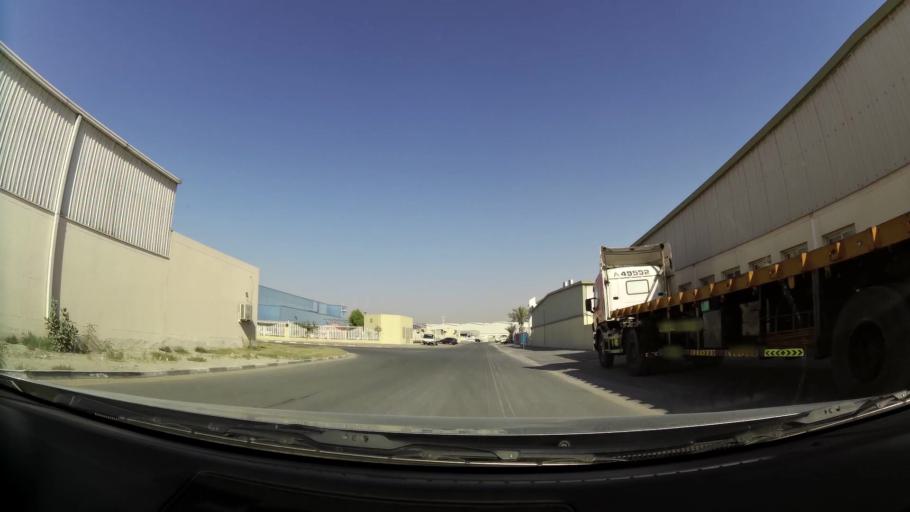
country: AE
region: Dubai
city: Dubai
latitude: 24.9871
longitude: 55.1131
